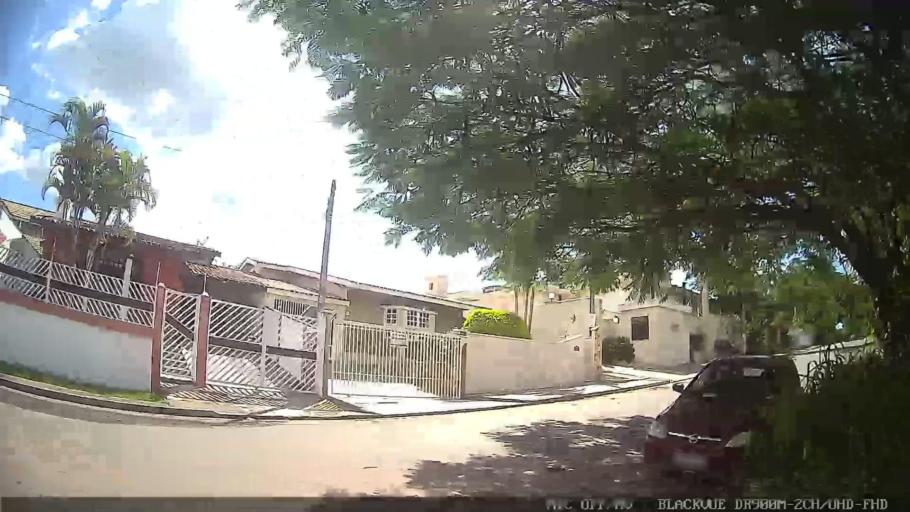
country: BR
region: Sao Paulo
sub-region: Atibaia
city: Atibaia
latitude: -23.1446
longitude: -46.5613
